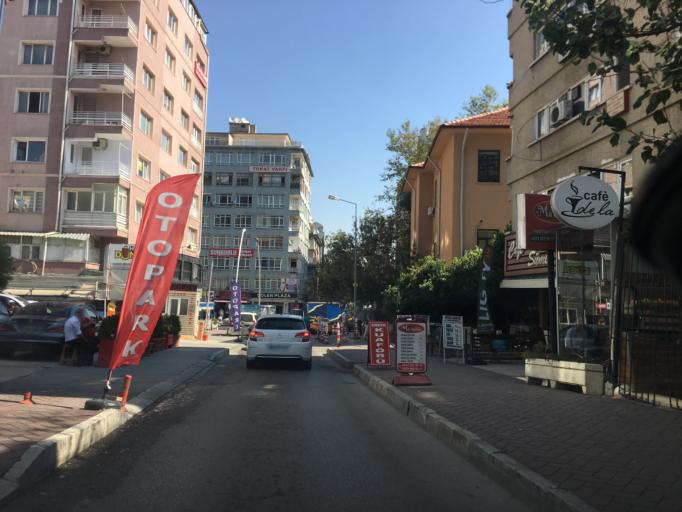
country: TR
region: Ankara
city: Ankara
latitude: 39.9220
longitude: 32.8499
